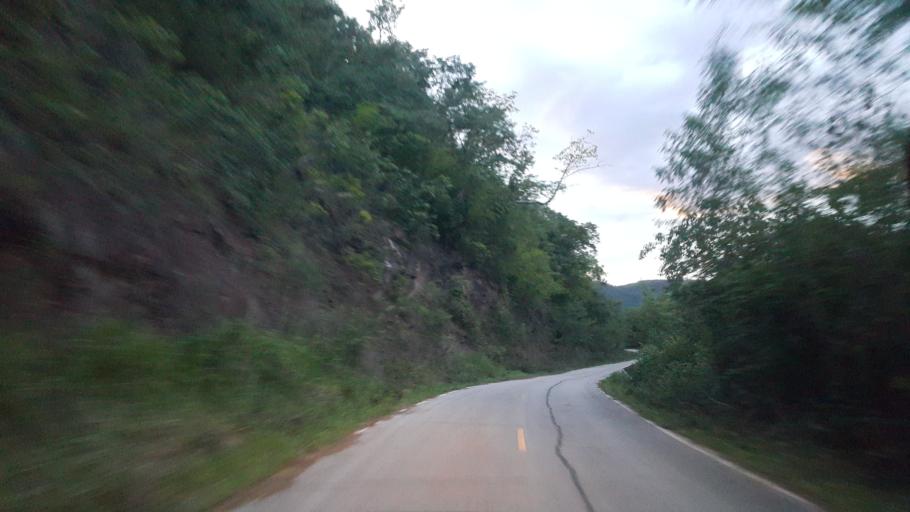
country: TH
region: Loei
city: Phu Ruea
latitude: 17.5268
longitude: 101.2280
